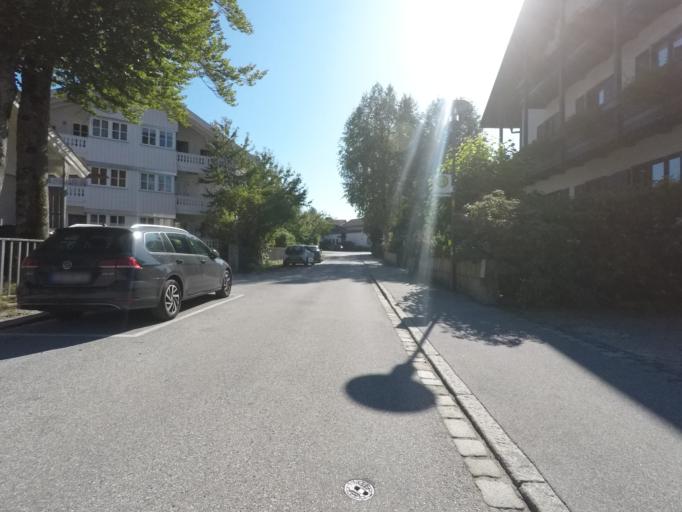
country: DE
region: Bavaria
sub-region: Upper Bavaria
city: Bad Toelz
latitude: 47.7618
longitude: 11.5475
